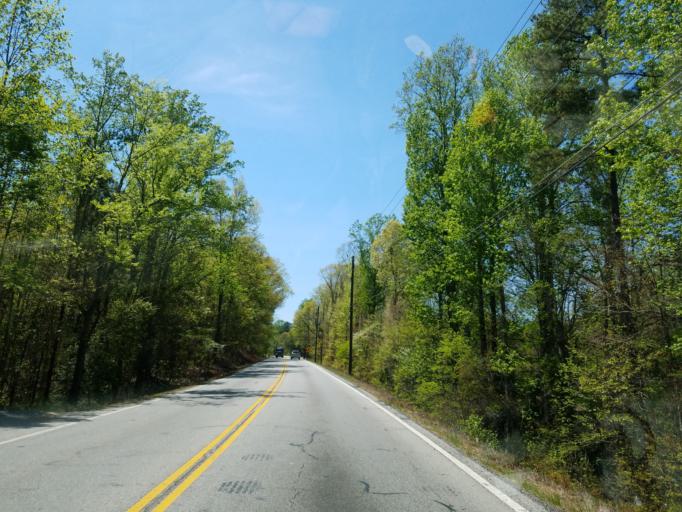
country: US
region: Georgia
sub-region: Paulding County
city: Hiram
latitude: 33.8687
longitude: -84.7834
